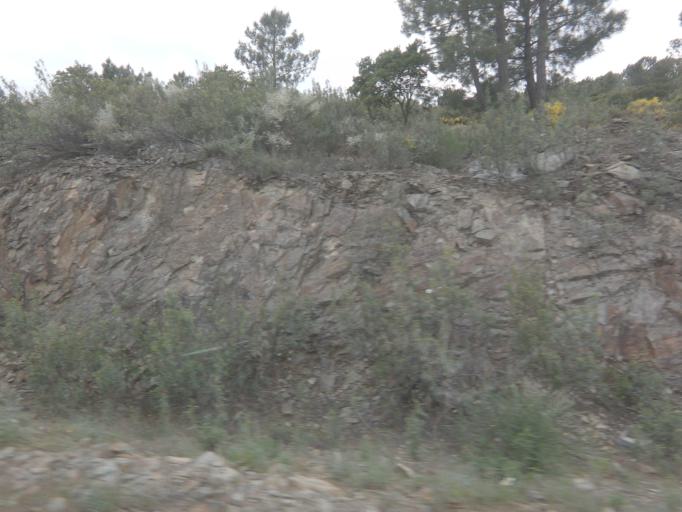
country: ES
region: Extremadura
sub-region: Provincia de Caceres
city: Acebo
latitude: 40.2228
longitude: -6.6730
